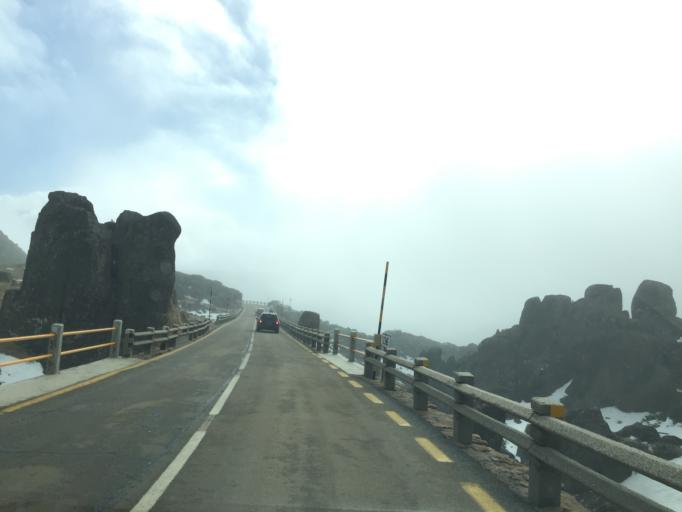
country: PT
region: Guarda
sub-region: Manteigas
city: Manteigas
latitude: 40.3227
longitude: -7.6029
